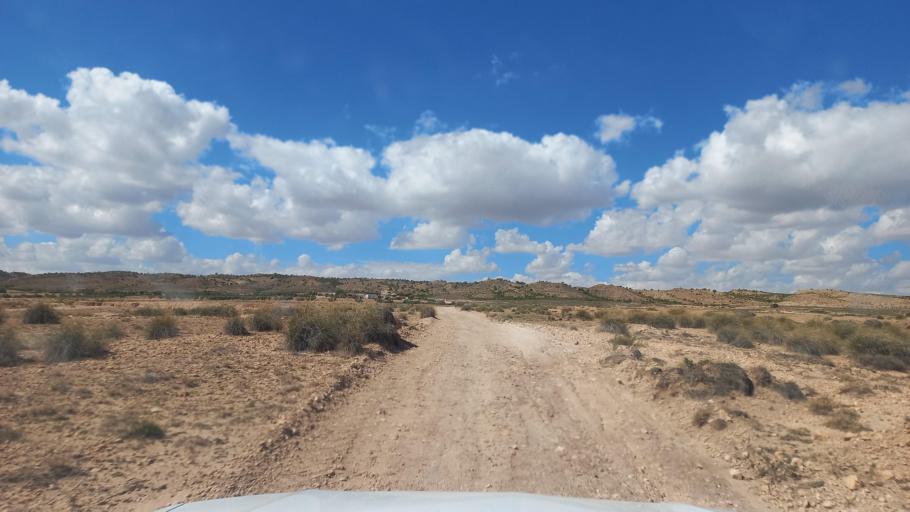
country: TN
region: Al Qasrayn
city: Sbiba
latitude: 35.3613
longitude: 9.0036
